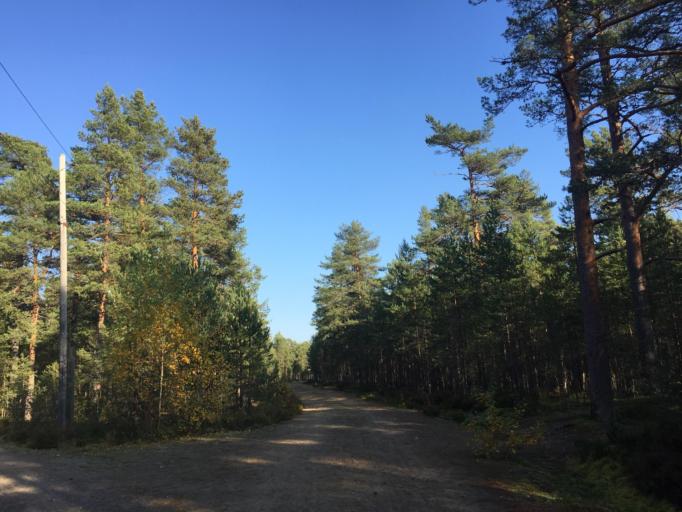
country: RU
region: Leningrad
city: Priozersk
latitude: 61.2810
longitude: 30.1017
